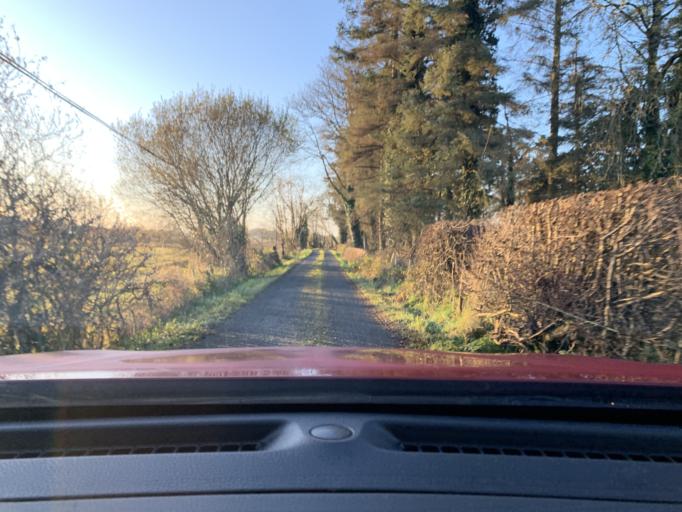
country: IE
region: Connaught
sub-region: Sligo
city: Ballymote
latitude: 54.0799
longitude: -8.5464
